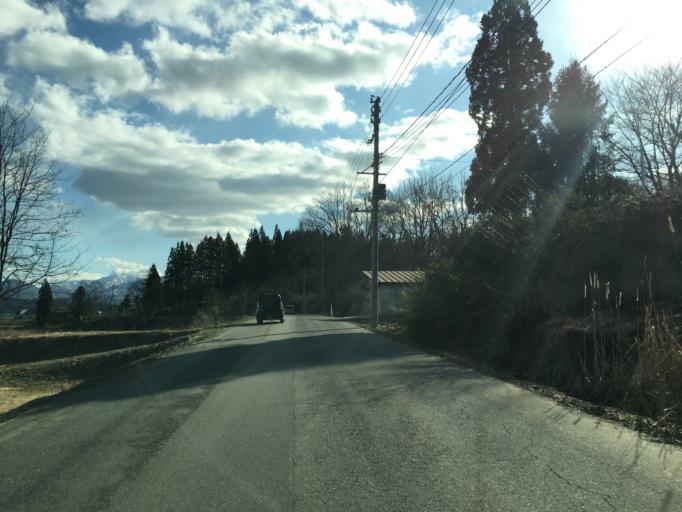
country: JP
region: Yamagata
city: Yonezawa
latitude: 37.9703
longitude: 139.9927
